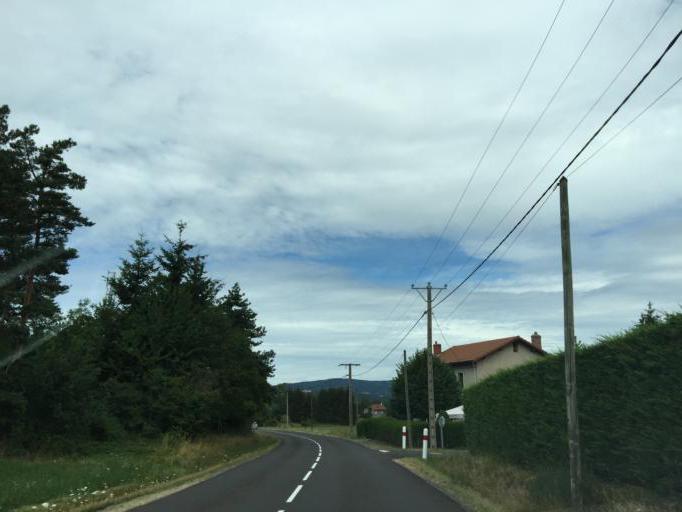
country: FR
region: Rhone-Alpes
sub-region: Departement de la Loire
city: Perigneux
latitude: 45.4070
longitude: 4.1329
